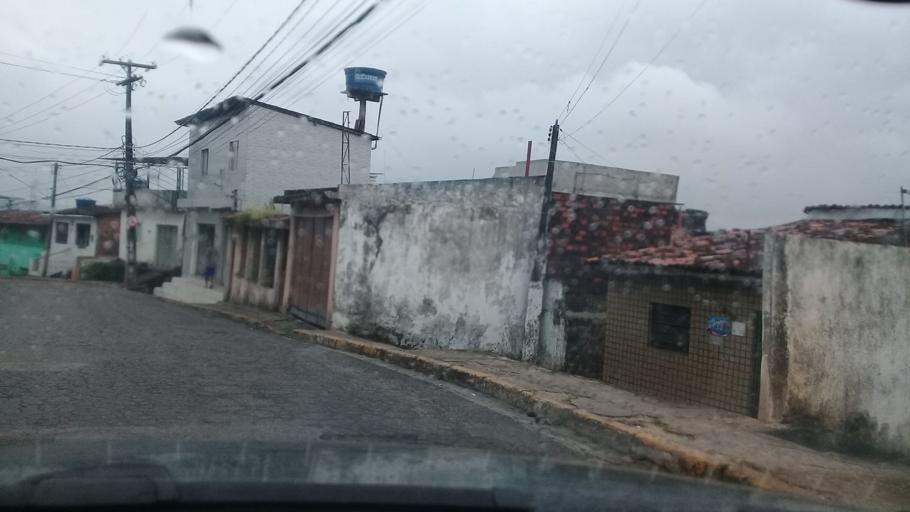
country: BR
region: Pernambuco
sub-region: Jaboatao Dos Guararapes
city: Jaboatao dos Guararapes
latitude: -8.0847
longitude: -34.9761
